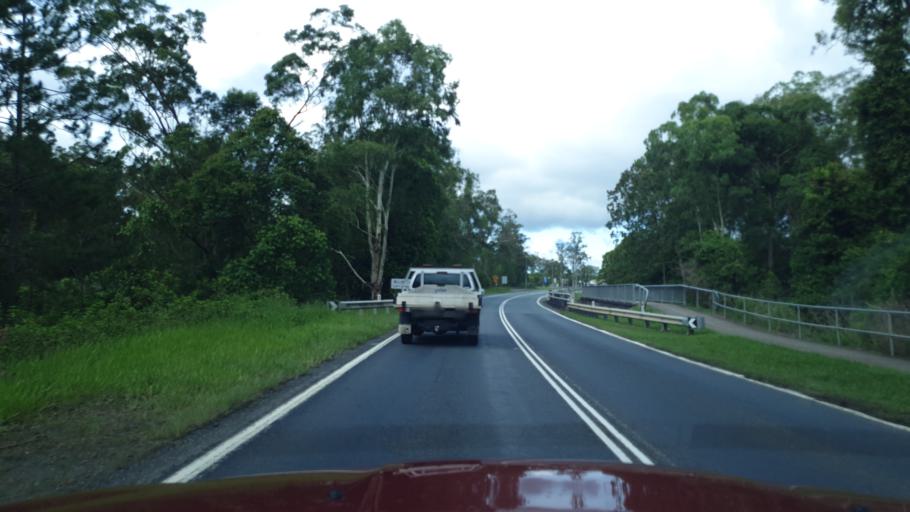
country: AU
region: Queensland
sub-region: Sunshine Coast
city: Little Mountain
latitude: -26.8146
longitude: 152.9637
